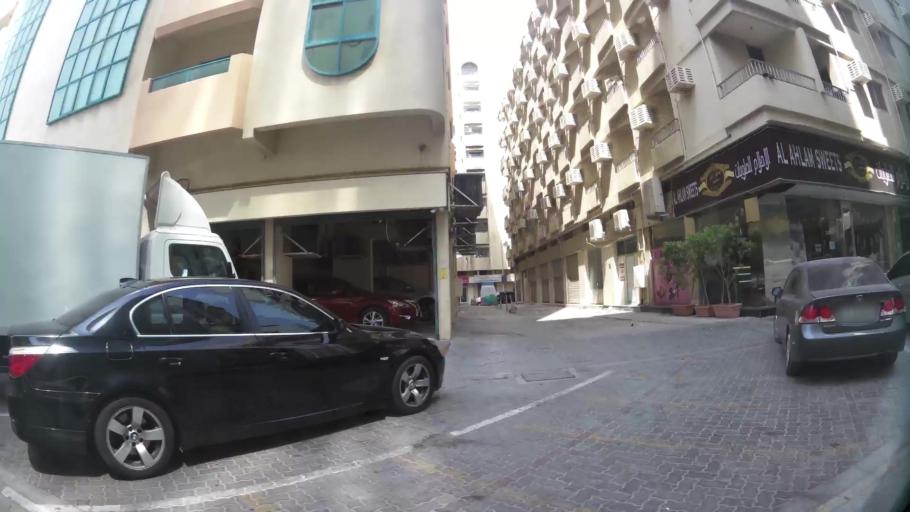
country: AE
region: Ash Shariqah
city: Sharjah
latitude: 25.3376
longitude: 55.3873
